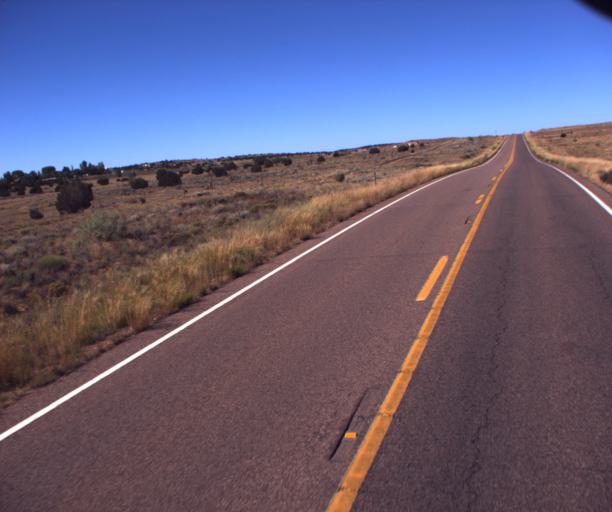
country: US
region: Arizona
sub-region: Navajo County
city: Snowflake
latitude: 34.5129
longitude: -110.1404
